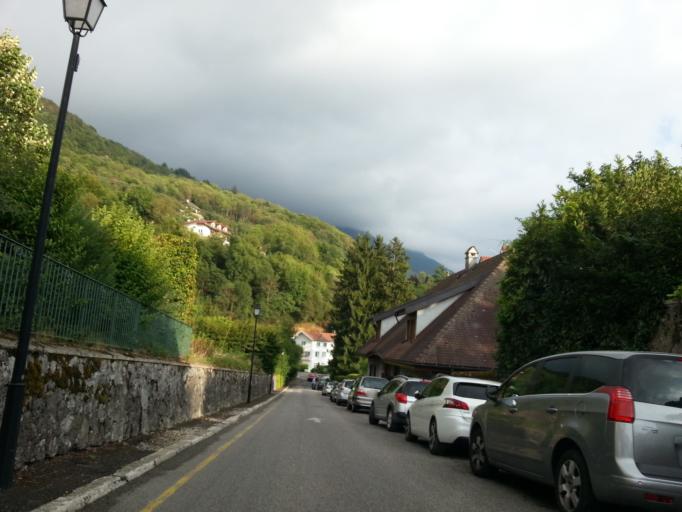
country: FR
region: Rhone-Alpes
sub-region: Departement de la Haute-Savoie
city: Talloires
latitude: 45.8377
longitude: 6.2158
